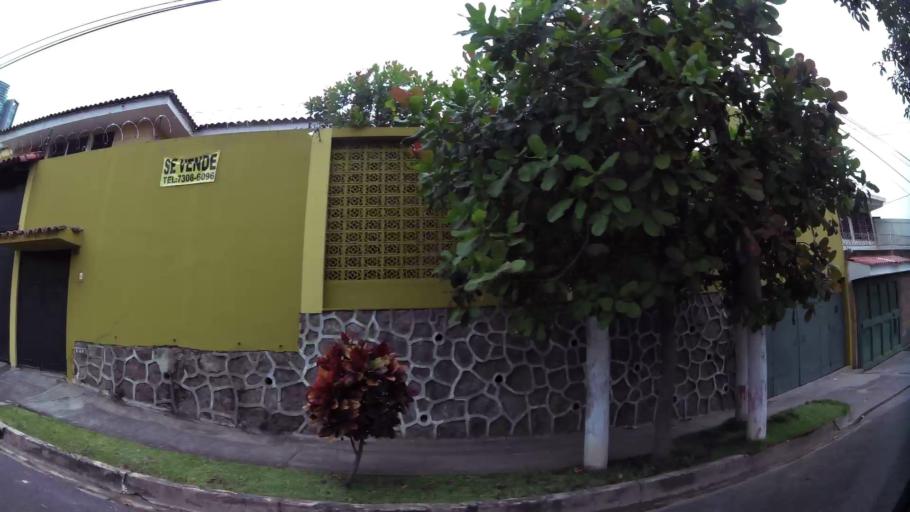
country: SV
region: San Salvador
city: Mejicanos
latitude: 13.7077
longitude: -89.2393
